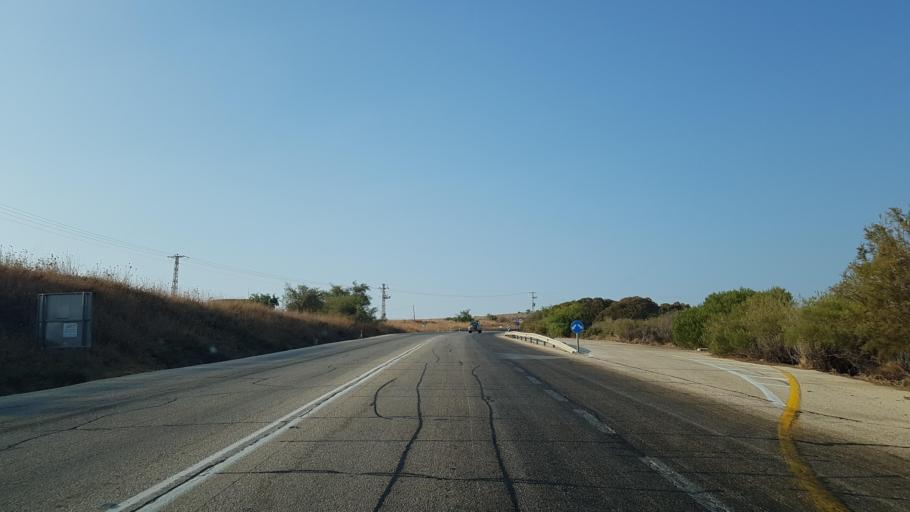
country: SY
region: Quneitra
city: Al Butayhah
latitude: 32.9052
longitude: 35.5975
